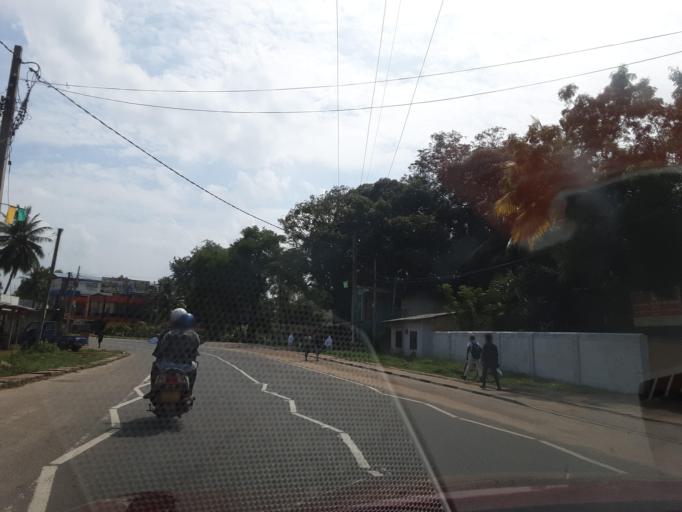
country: LK
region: Northern Province
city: Vavuniya
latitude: 8.5366
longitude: 80.4941
